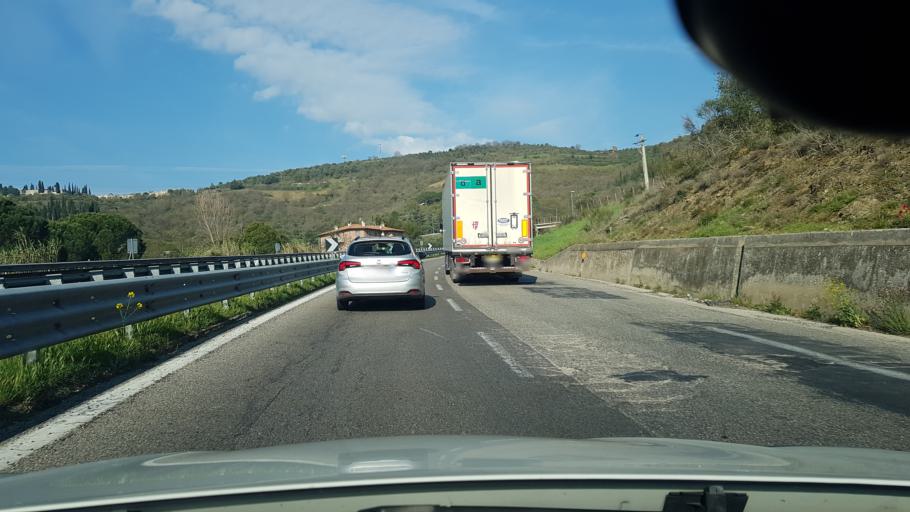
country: IT
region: Umbria
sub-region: Provincia di Perugia
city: Magione
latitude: 43.1517
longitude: 12.2118
